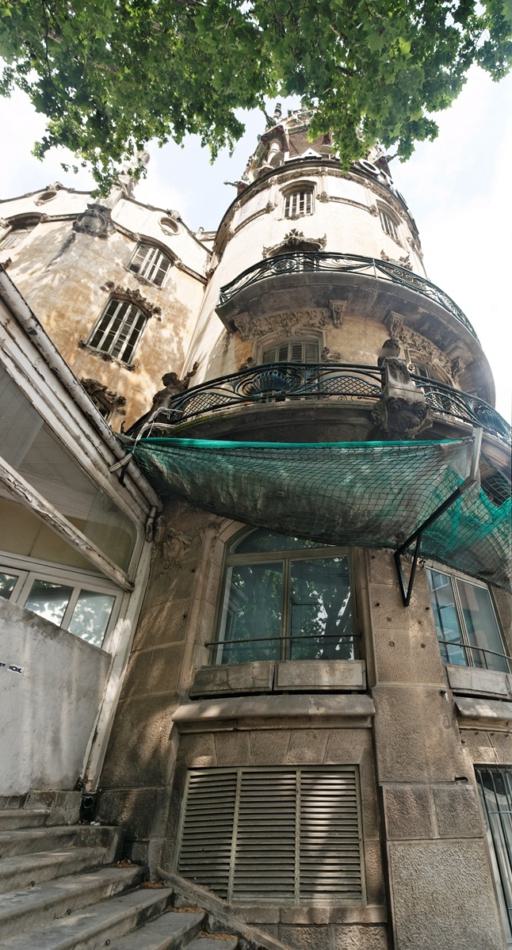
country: ES
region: Catalonia
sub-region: Provincia de Barcelona
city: Sarria-Sant Gervasi
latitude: 41.4103
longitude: 2.1371
